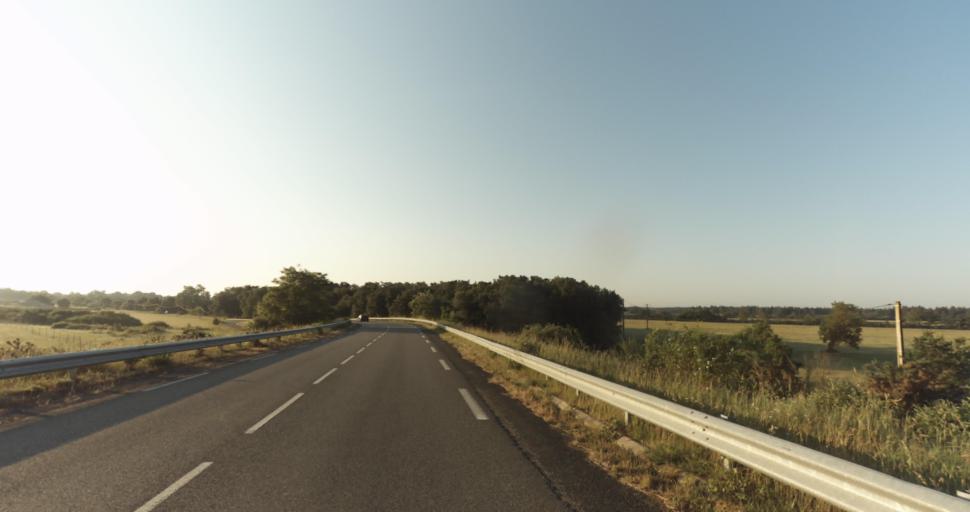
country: FR
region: Midi-Pyrenees
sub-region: Departement de la Haute-Garonne
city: Fontenilles
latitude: 43.5810
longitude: 1.2044
